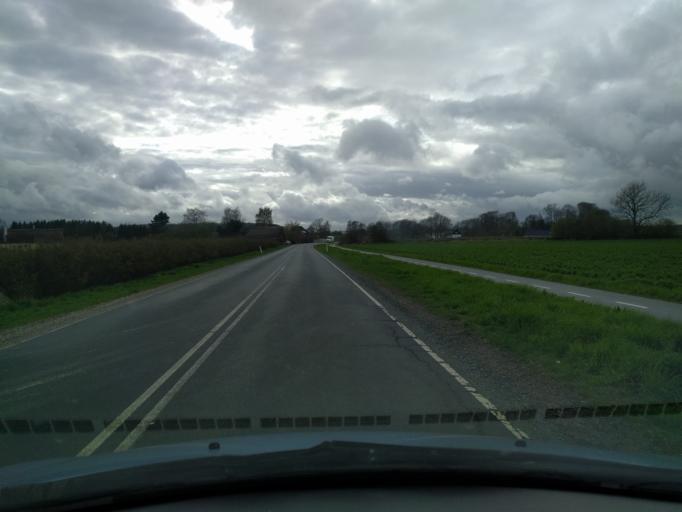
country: DK
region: South Denmark
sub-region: Kerteminde Kommune
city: Langeskov
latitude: 55.4051
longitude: 10.5665
